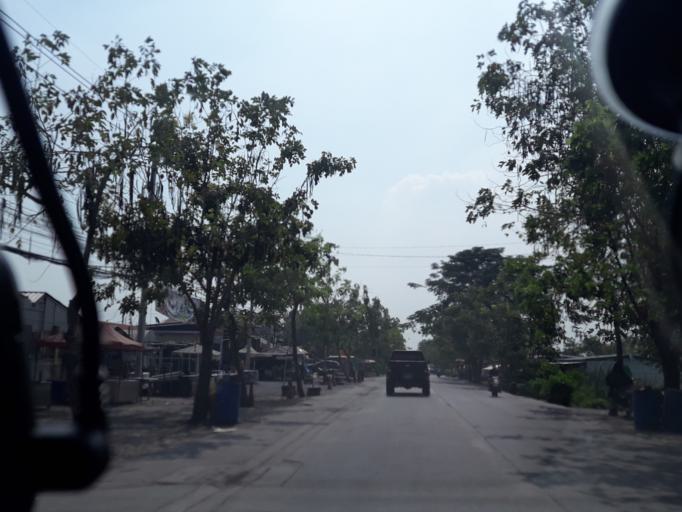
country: TH
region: Bangkok
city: Khlong Sam Wa
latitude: 13.8410
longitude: 100.7130
